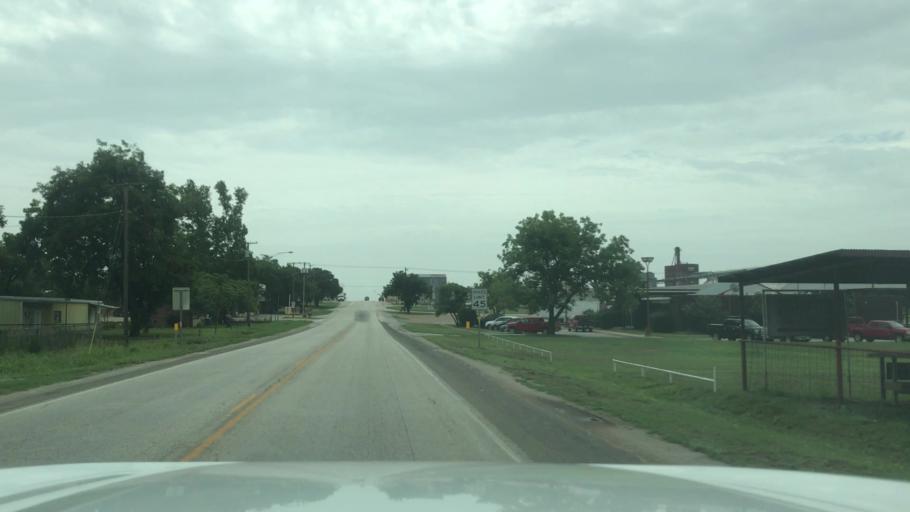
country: US
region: Texas
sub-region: Eastland County
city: Gorman
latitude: 32.2126
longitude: -98.6693
